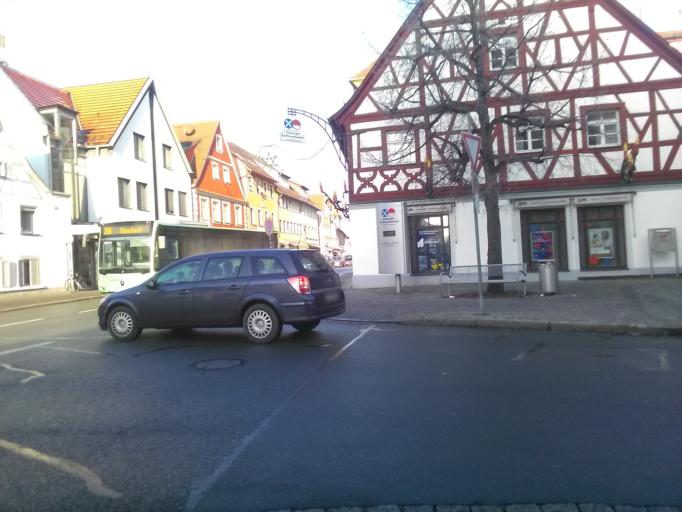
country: DE
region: Bavaria
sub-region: Upper Franconia
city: Forchheim
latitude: 49.7168
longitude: 11.0603
